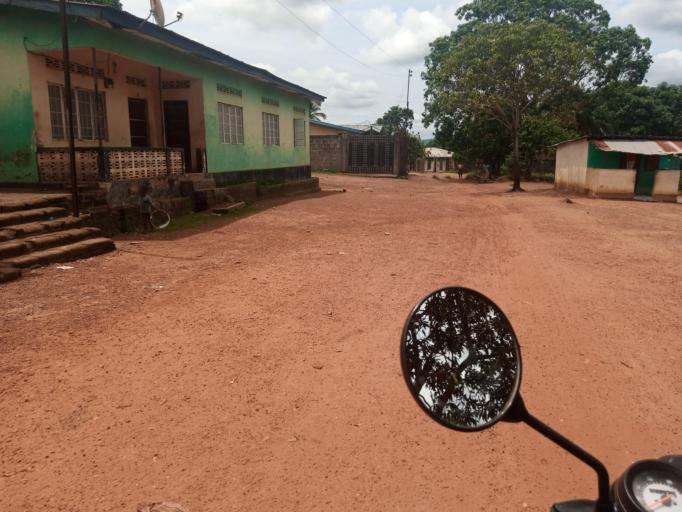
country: SL
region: Southern Province
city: Bo
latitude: 7.9533
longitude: -11.7184
